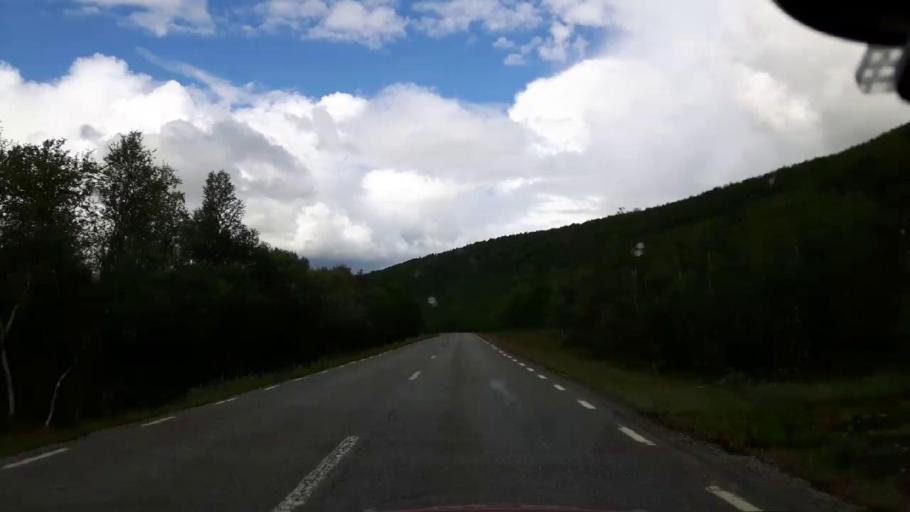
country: NO
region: Nordland
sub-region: Hattfjelldal
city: Hattfjelldal
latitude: 65.0654
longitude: 14.6902
